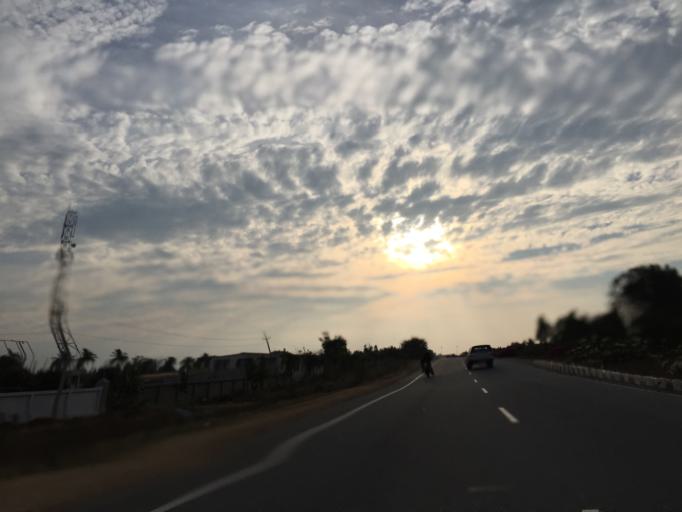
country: IN
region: Karnataka
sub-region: Kolar
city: Kolar
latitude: 13.1451
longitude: 78.2426
